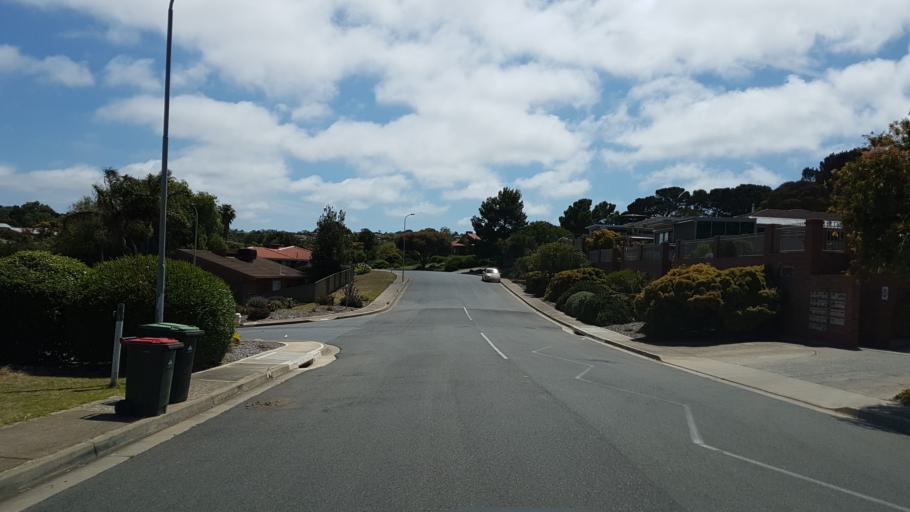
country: AU
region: South Australia
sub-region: Marion
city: Happy Valley
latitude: -35.0752
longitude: 138.5177
